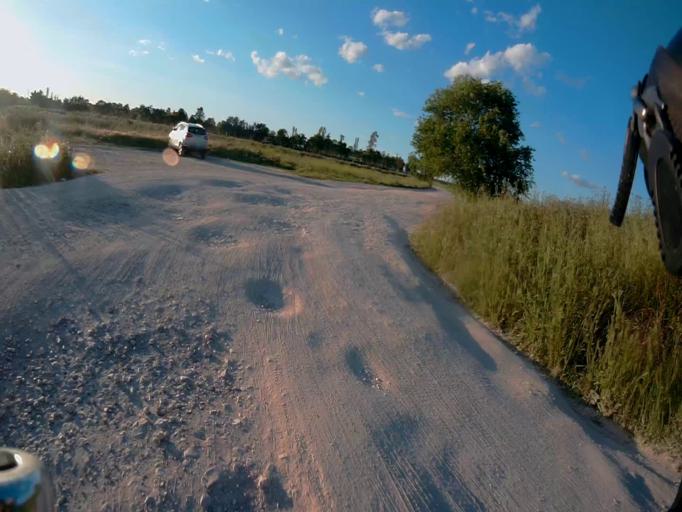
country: ES
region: Madrid
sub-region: Provincia de Madrid
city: Leganes
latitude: 40.3276
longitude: -3.7953
